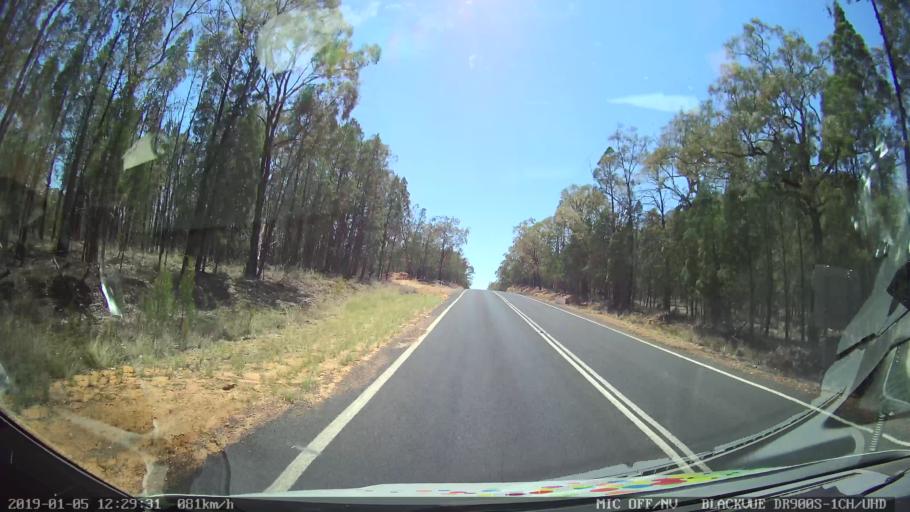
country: AU
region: New South Wales
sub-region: Warrumbungle Shire
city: Coonabarabran
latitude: -31.2327
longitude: 149.3382
